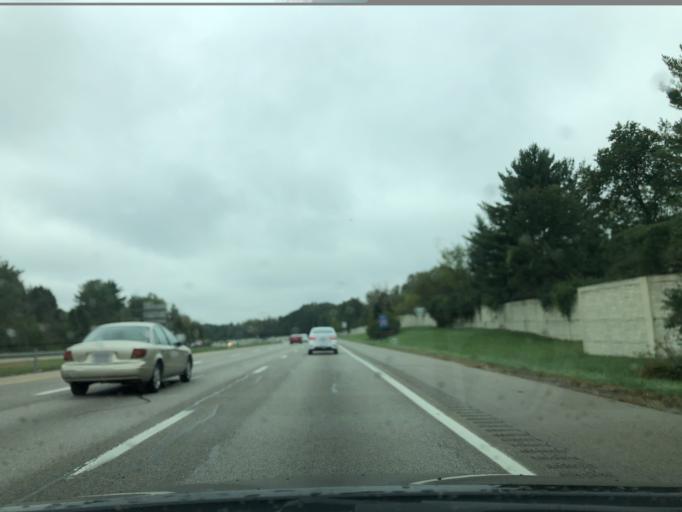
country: US
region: Ohio
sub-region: Hamilton County
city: Sixteen Mile Stand
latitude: 39.2561
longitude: -84.3313
